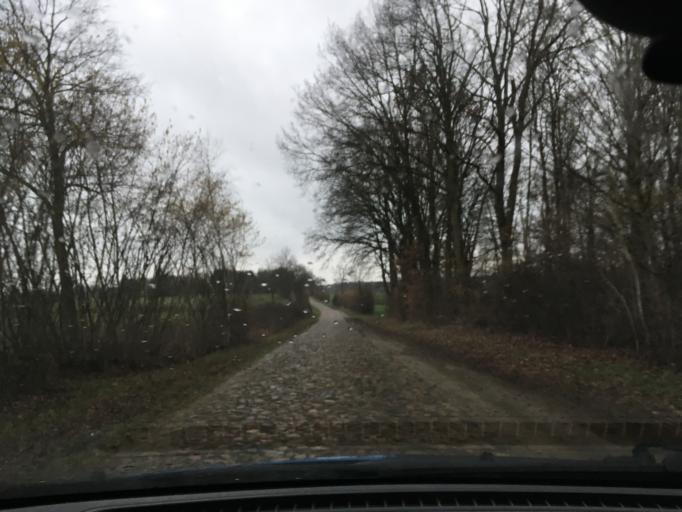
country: DE
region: Schleswig-Holstein
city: Kruzen
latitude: 53.4143
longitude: 10.5274
